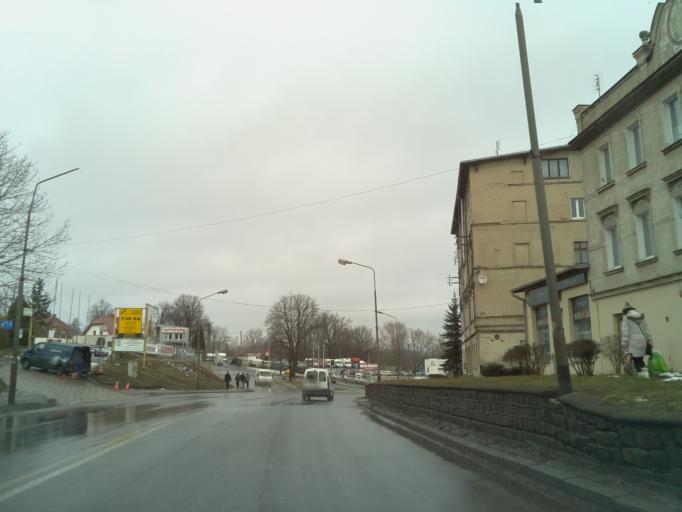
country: PL
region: Lower Silesian Voivodeship
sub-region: Powiat walbrzyski
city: Szczawno-Zdroj
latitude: 50.8113
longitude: 16.2961
